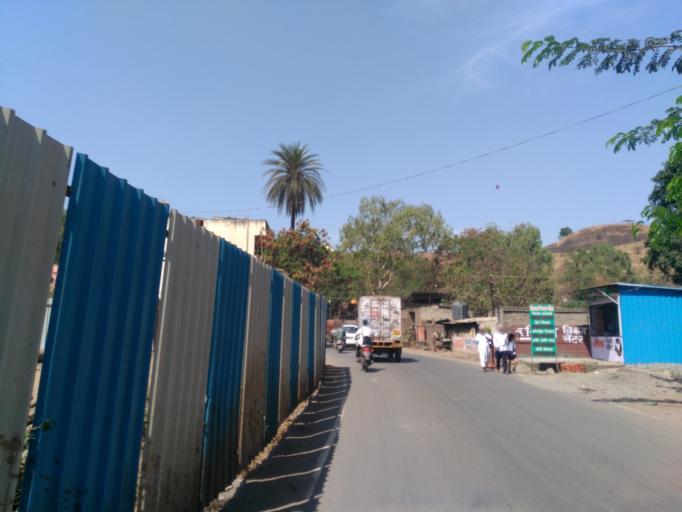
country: IN
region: Maharashtra
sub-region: Pune Division
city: Pune
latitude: 18.4384
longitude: 73.8617
